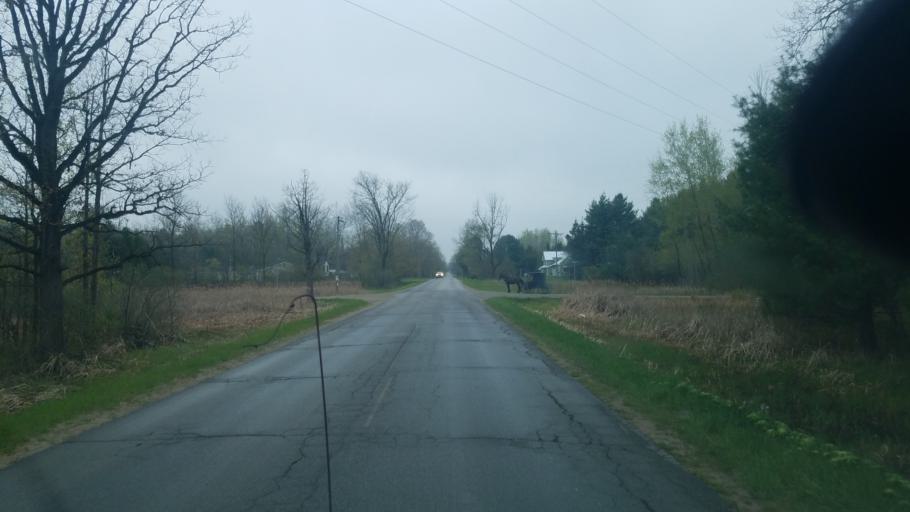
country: US
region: Michigan
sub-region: Mecosta County
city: Canadian Lakes
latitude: 43.5261
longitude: -85.2842
